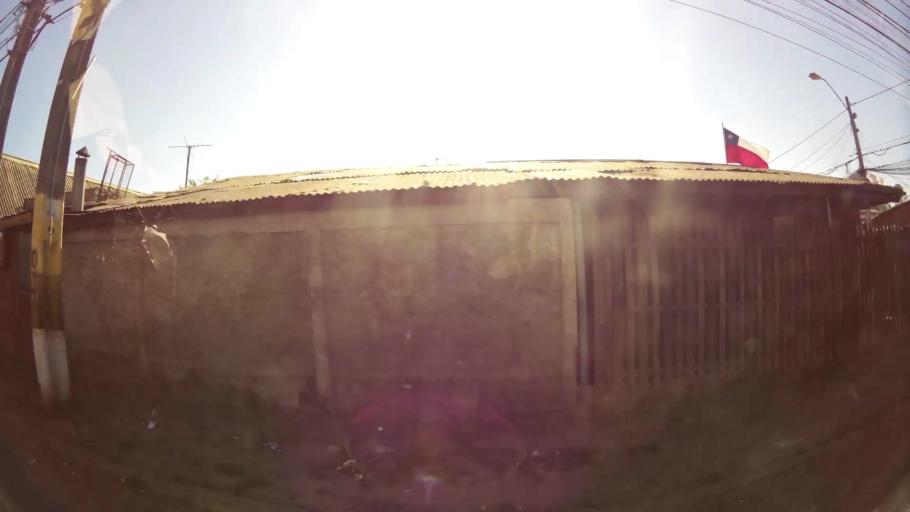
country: CL
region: Santiago Metropolitan
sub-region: Provincia de Talagante
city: Penaflor
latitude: -33.6087
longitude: -70.8718
